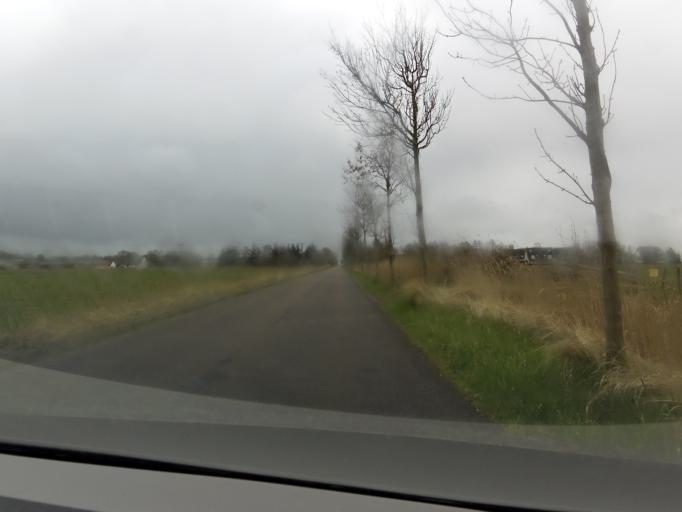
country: DE
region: Mecklenburg-Vorpommern
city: Zingst
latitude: 54.4289
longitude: 12.7370
